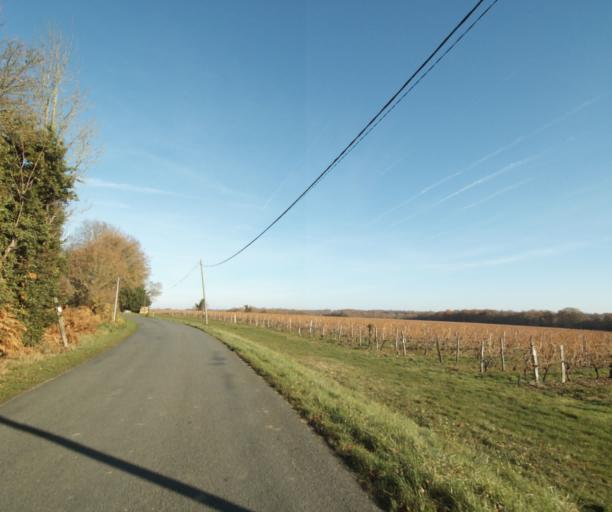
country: FR
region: Poitou-Charentes
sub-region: Departement de la Charente-Maritime
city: Cherac
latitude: 45.7153
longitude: -0.4532
